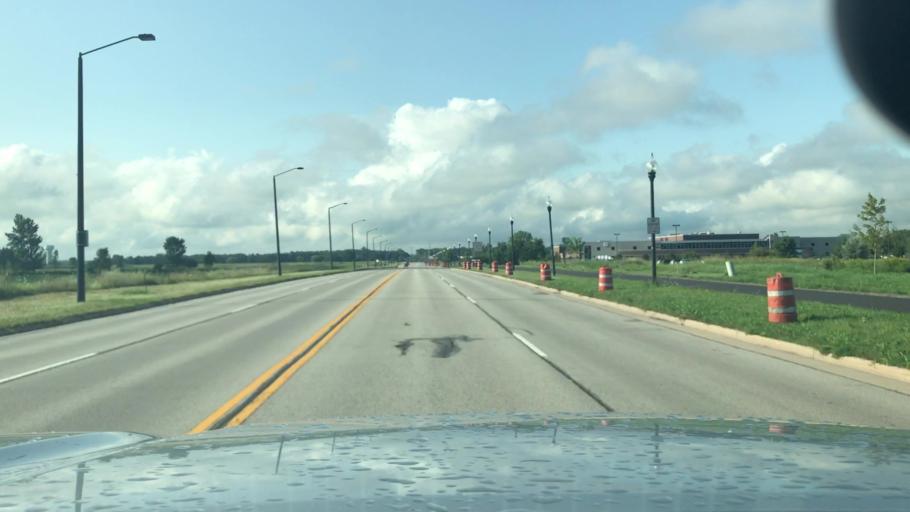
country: US
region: Wisconsin
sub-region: Brown County
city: Bellevue
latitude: 44.4717
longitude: -87.9171
